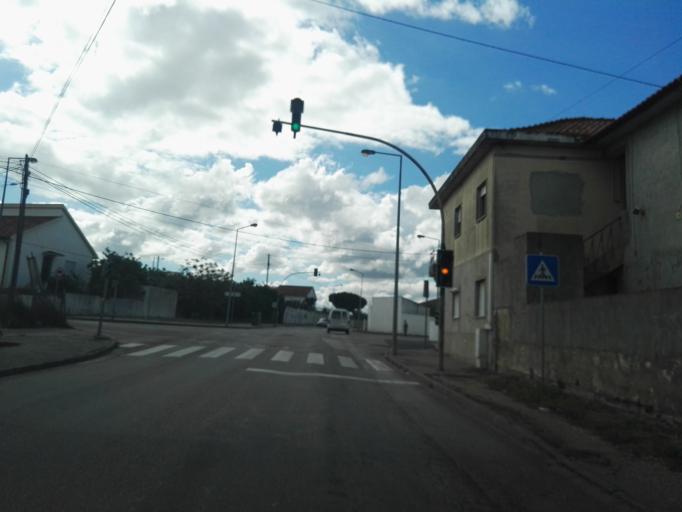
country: PT
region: Santarem
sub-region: Torres Novas
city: Riachos
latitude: 39.4483
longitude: -8.5121
